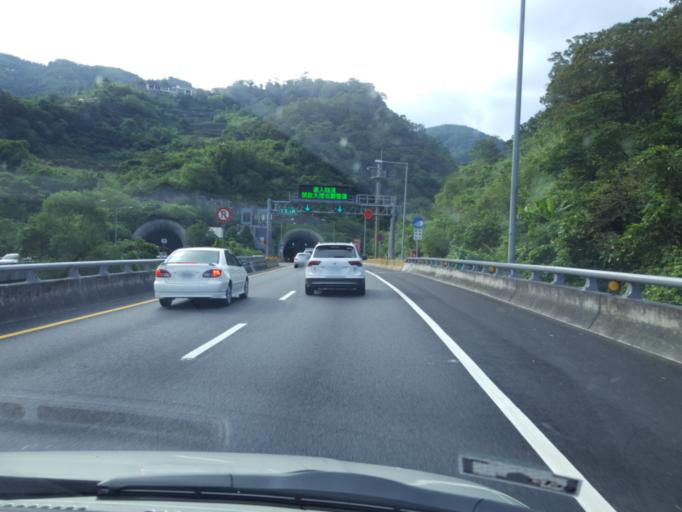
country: TW
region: Taiwan
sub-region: Keelung
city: Keelung
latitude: 24.9492
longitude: 121.7027
